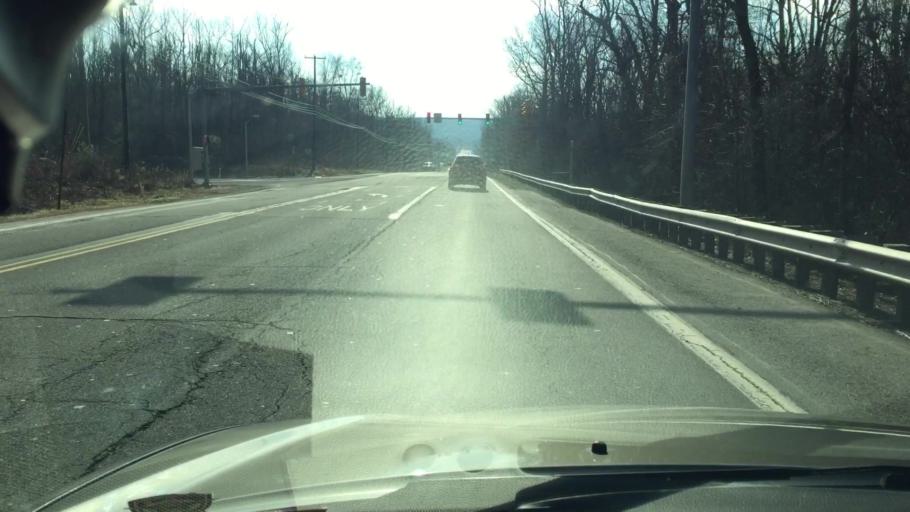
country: US
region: Pennsylvania
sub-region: Luzerne County
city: Mountain Top
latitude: 41.1336
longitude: -75.9043
